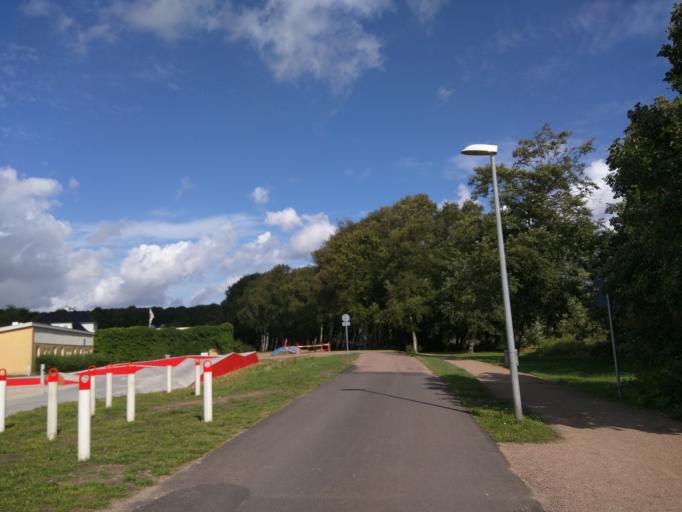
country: DK
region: Central Jutland
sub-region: Viborg Kommune
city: Viborg
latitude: 56.4374
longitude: 9.4057
